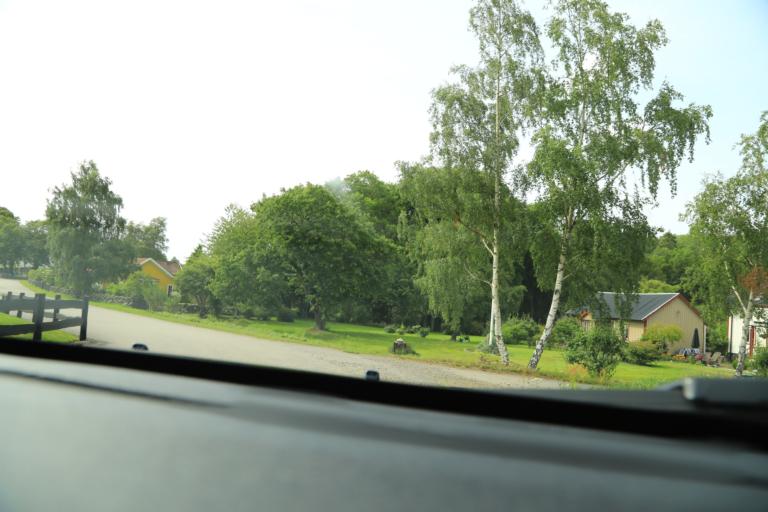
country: SE
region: Halland
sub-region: Varbergs Kommun
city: Veddige
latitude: 57.1898
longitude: 12.2819
